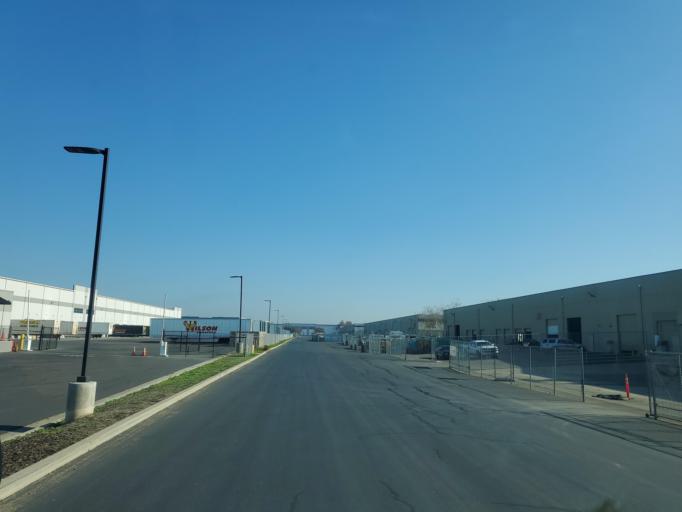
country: US
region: California
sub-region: San Joaquin County
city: Kennedy
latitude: 37.9066
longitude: -121.2440
